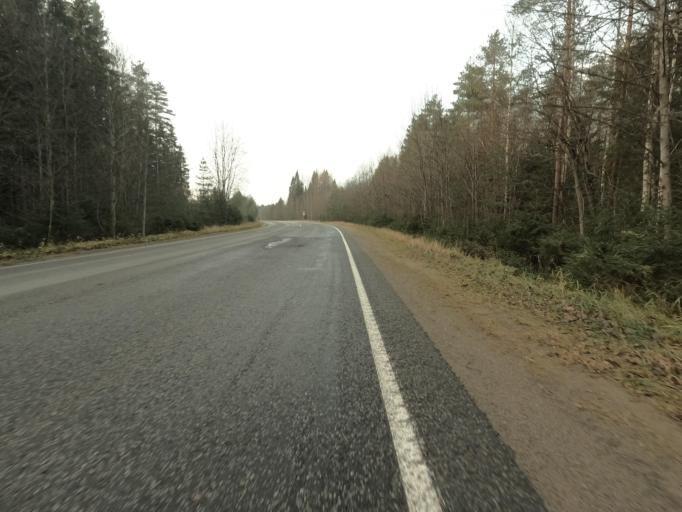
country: RU
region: Leningrad
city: Kirovsk
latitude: 59.8242
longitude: 30.9818
